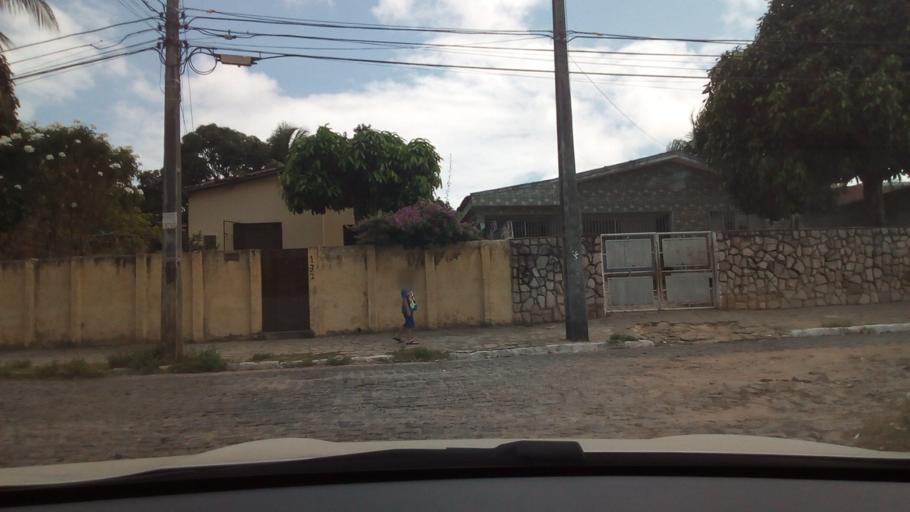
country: BR
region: Paraiba
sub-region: Joao Pessoa
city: Joao Pessoa
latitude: -7.1471
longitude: -34.8313
